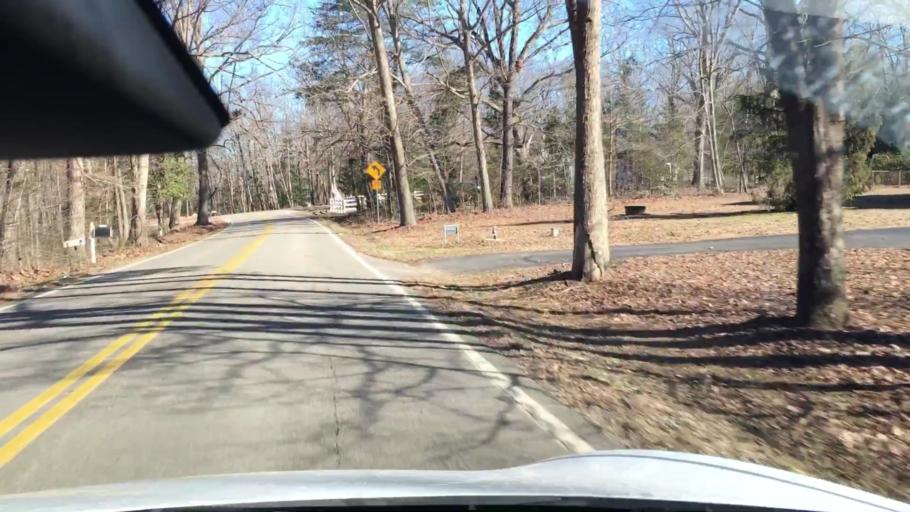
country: US
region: Virginia
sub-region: Powhatan County
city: Powhatan
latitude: 37.5439
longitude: -77.7944
